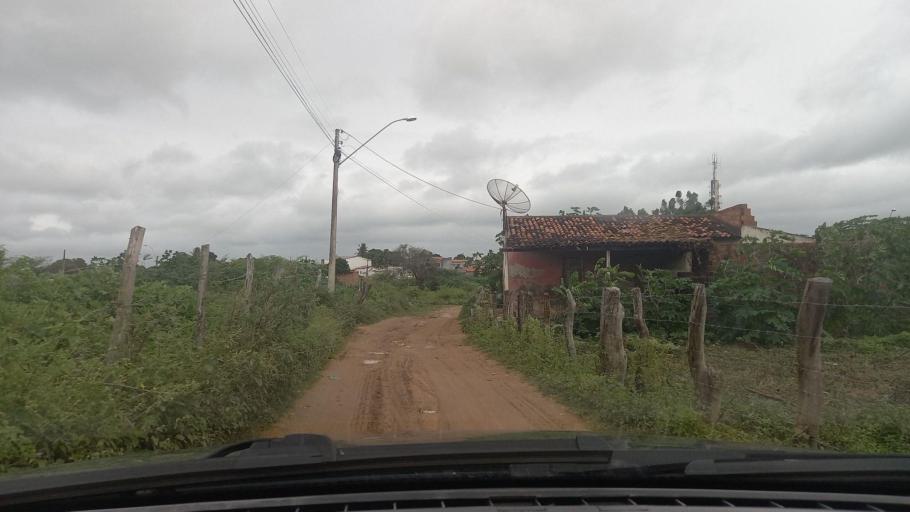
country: BR
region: Alagoas
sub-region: Delmiro Gouveia
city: Delmiro Gouveia
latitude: -9.3889
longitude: -37.9944
